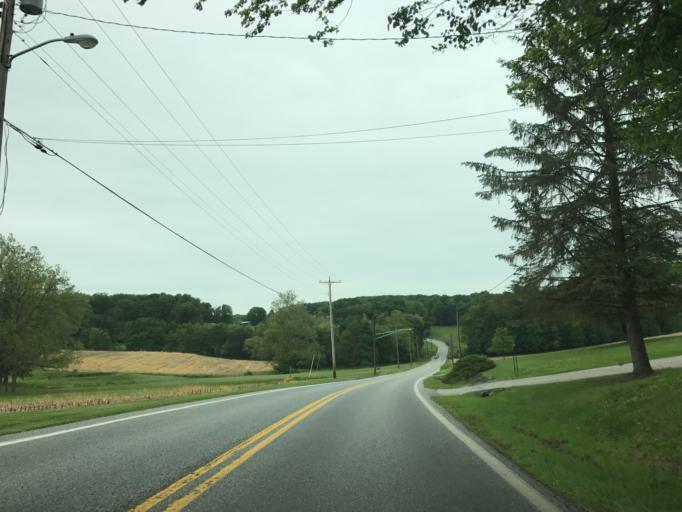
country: US
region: Pennsylvania
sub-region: York County
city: New Freedom
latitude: 39.7093
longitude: -76.6791
